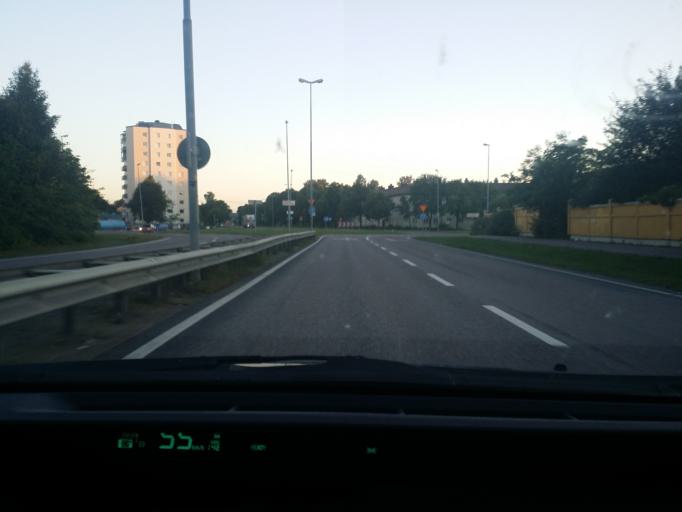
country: SE
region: Vaestmanland
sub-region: Vasteras
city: Vasteras
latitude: 59.6323
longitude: 16.5566
